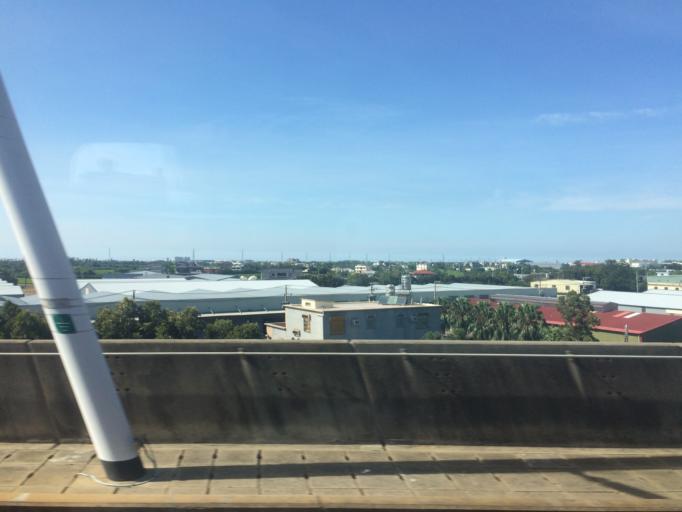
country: TW
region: Taiwan
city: Taoyuan City
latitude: 24.9515
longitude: 121.1406
